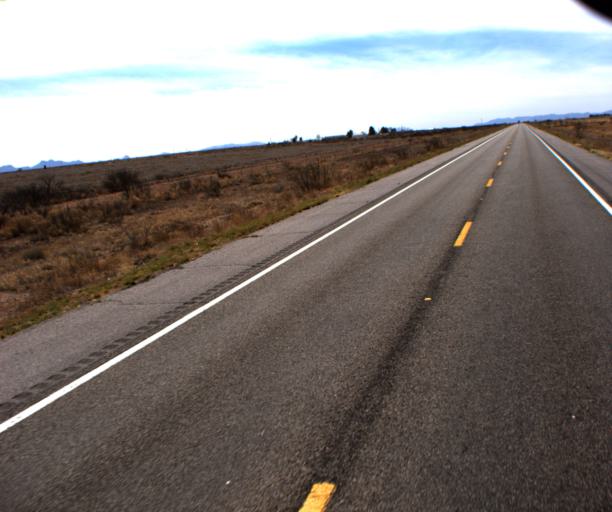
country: US
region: Arizona
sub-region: Cochise County
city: Pirtleville
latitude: 31.5829
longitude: -109.6688
